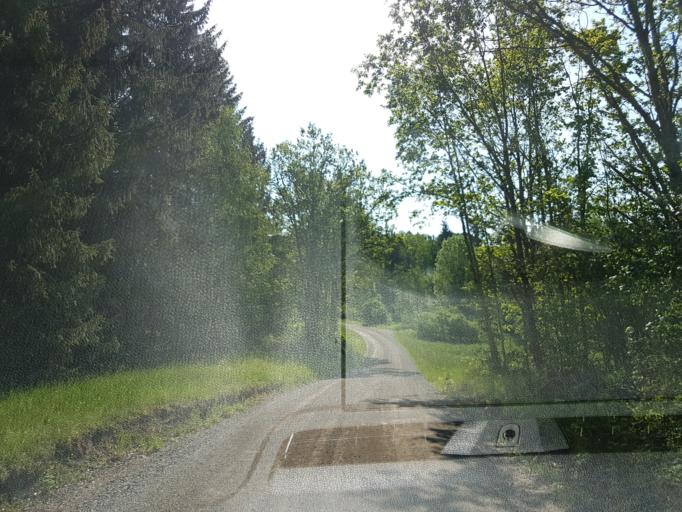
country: SE
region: OEstergoetland
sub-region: Atvidabergs Kommun
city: Atvidaberg
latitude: 58.1851
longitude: 16.1335
